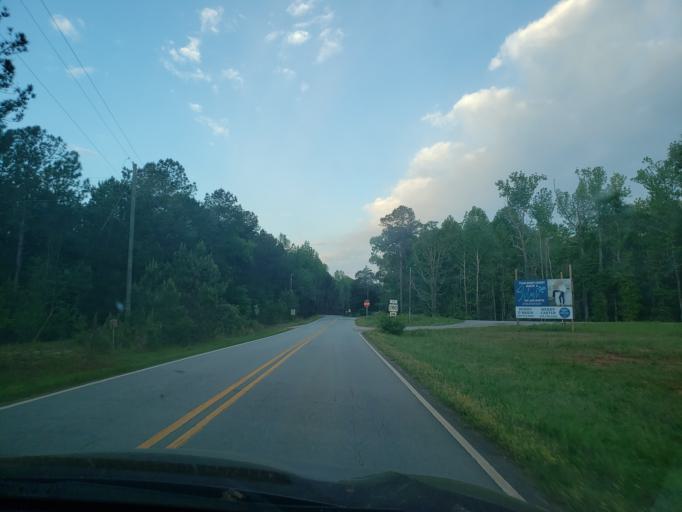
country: US
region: Alabama
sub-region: Tallapoosa County
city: Camp Hill
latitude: 32.7014
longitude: -85.7129
